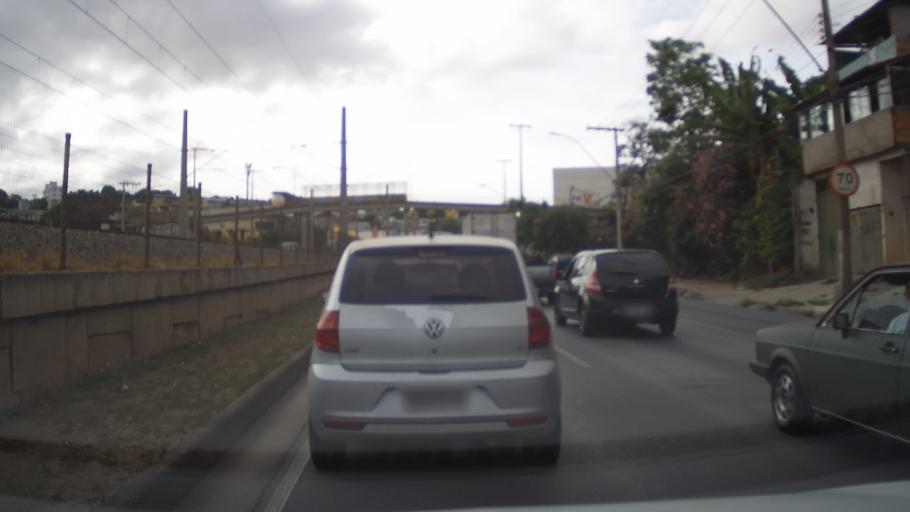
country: BR
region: Minas Gerais
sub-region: Belo Horizonte
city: Belo Horizonte
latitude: -19.8380
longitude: -43.9384
